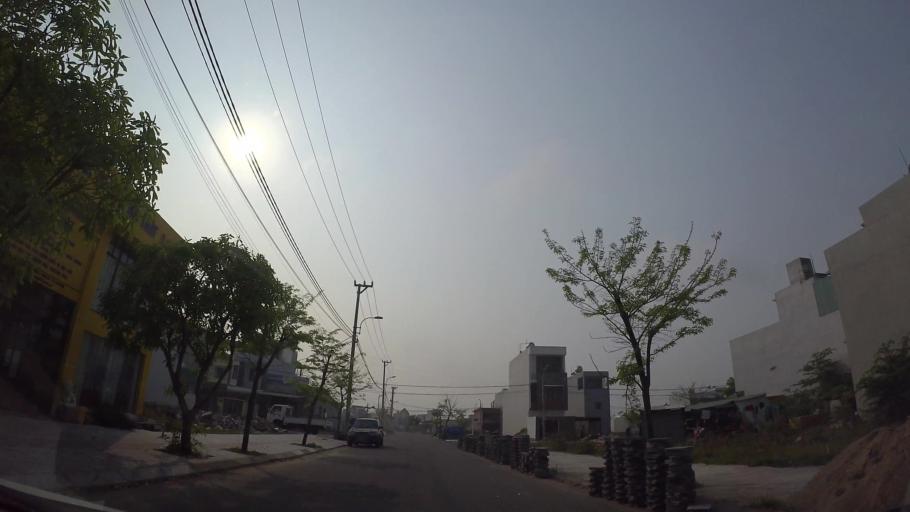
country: VN
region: Da Nang
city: Cam Le
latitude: 16.0099
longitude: 108.2244
